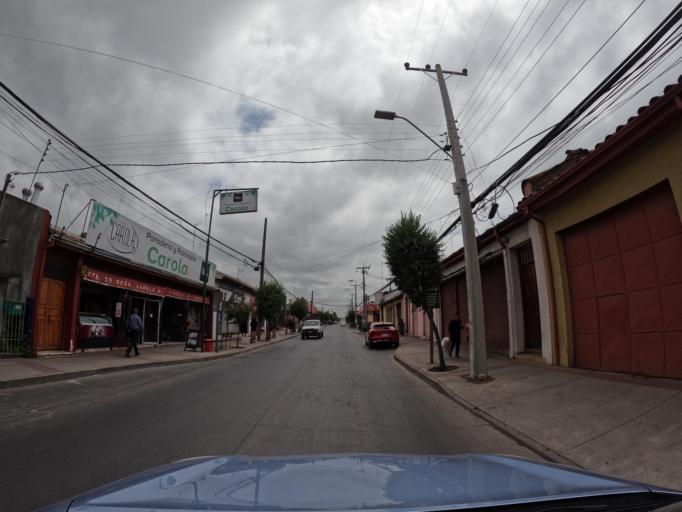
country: CL
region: O'Higgins
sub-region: Provincia de Colchagua
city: Chimbarongo
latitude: -34.7092
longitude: -71.0441
